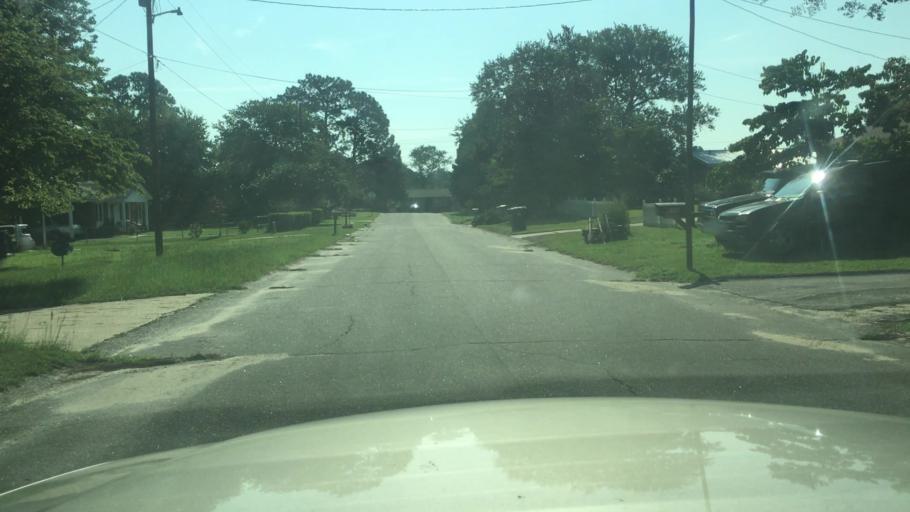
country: US
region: North Carolina
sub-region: Cumberland County
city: Spring Lake
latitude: 35.1540
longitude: -78.9210
